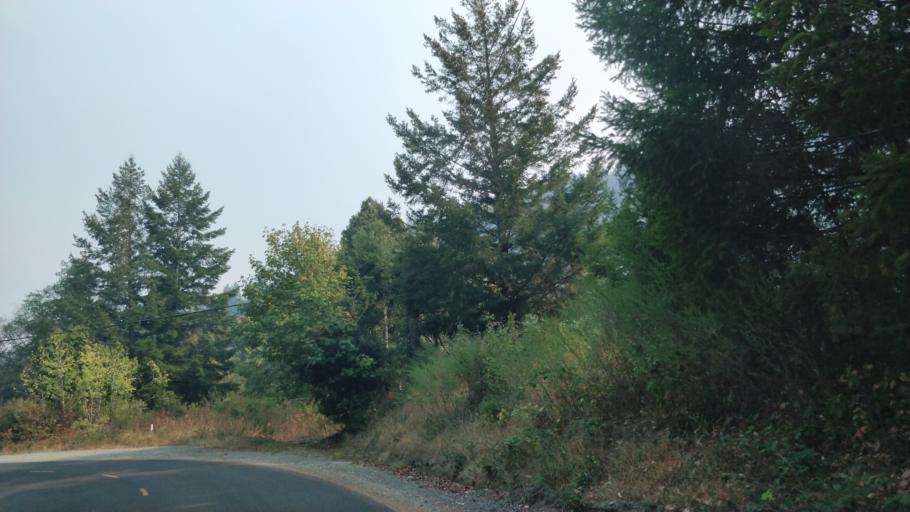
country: US
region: California
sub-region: Humboldt County
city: Rio Dell
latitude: 40.2687
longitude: -124.2285
